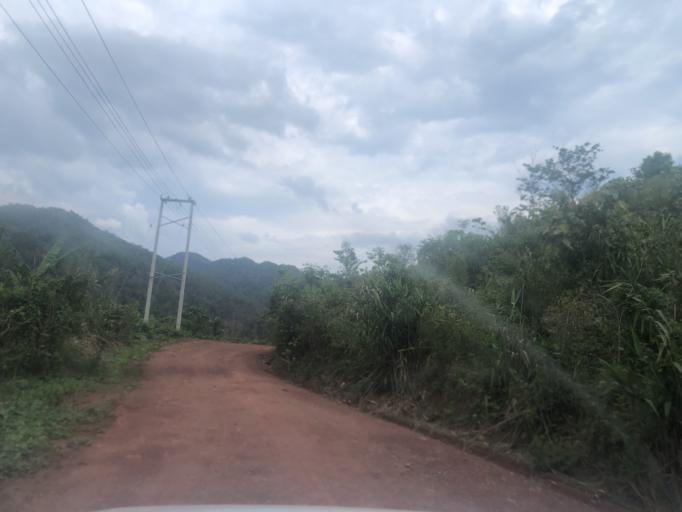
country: LA
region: Oudomxai
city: Muang La
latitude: 21.2624
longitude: 102.0042
